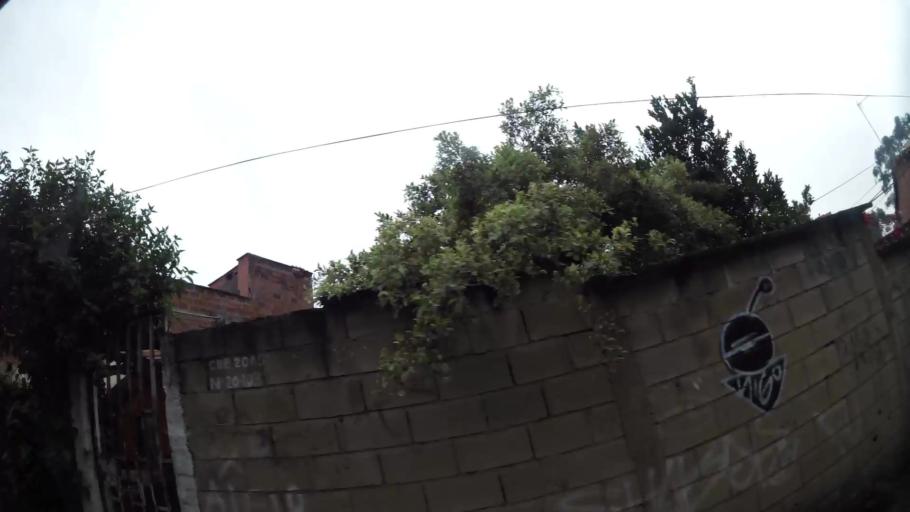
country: CO
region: Antioquia
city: Envigado
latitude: 6.1786
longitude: -75.5617
